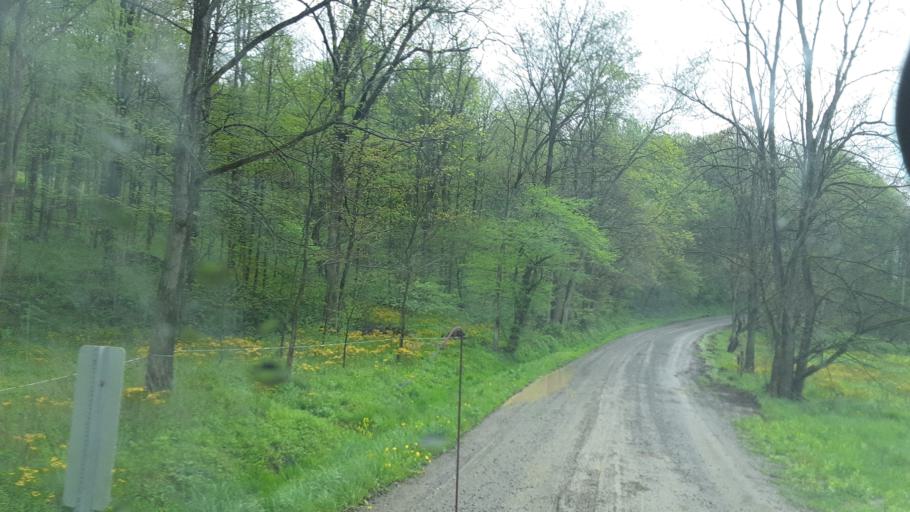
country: US
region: Ohio
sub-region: Holmes County
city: Millersburg
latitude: 40.4934
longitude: -81.8401
